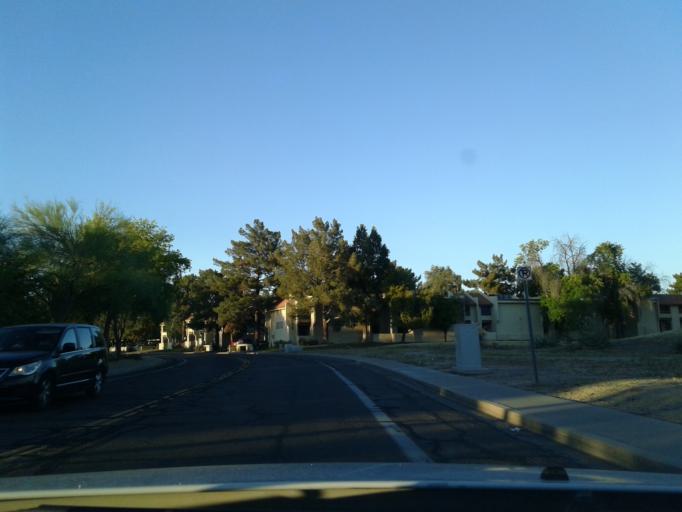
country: US
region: Arizona
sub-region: Maricopa County
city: Glendale
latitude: 33.5582
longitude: -112.1086
